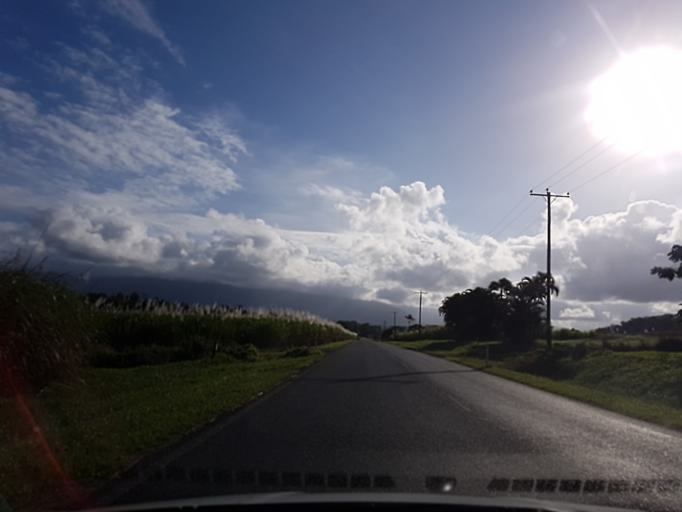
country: AU
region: Queensland
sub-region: Cairns
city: Port Douglas
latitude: -16.3929
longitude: 145.4045
